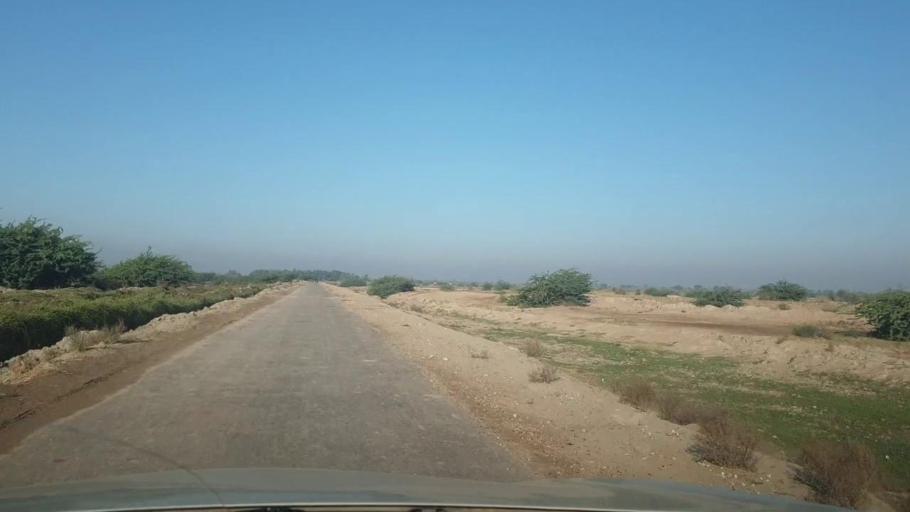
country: PK
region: Sindh
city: Bhan
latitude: 26.5500
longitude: 67.7021
